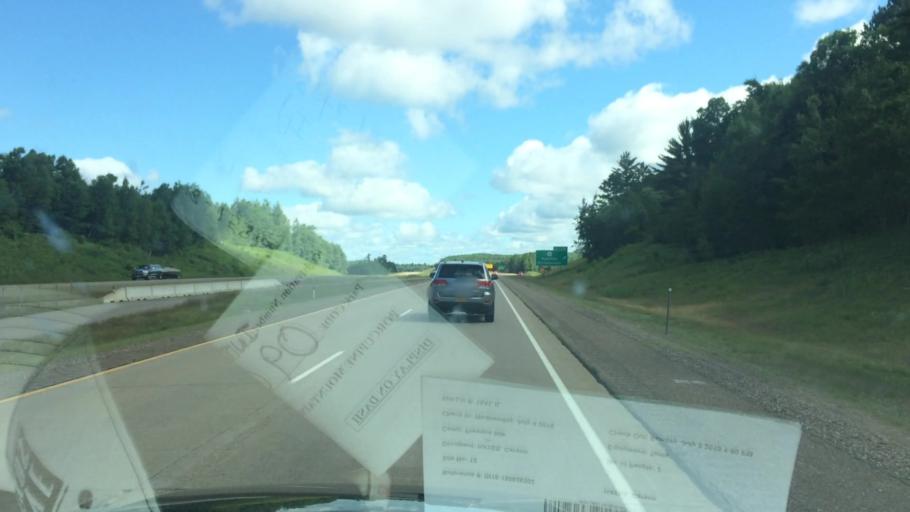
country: US
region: Wisconsin
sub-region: Lincoln County
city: Tomahawk
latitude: 45.5361
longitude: -89.6731
